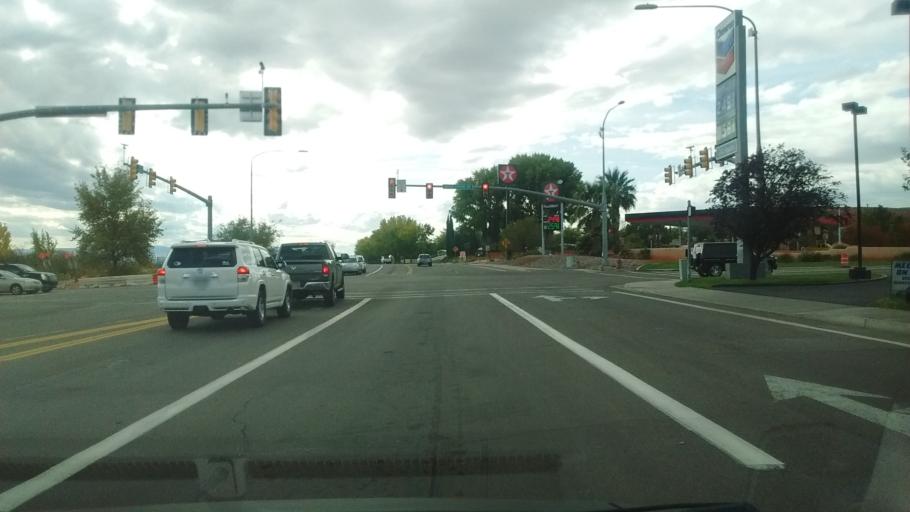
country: US
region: Utah
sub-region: Washington County
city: Washington
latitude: 37.1298
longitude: -113.5256
